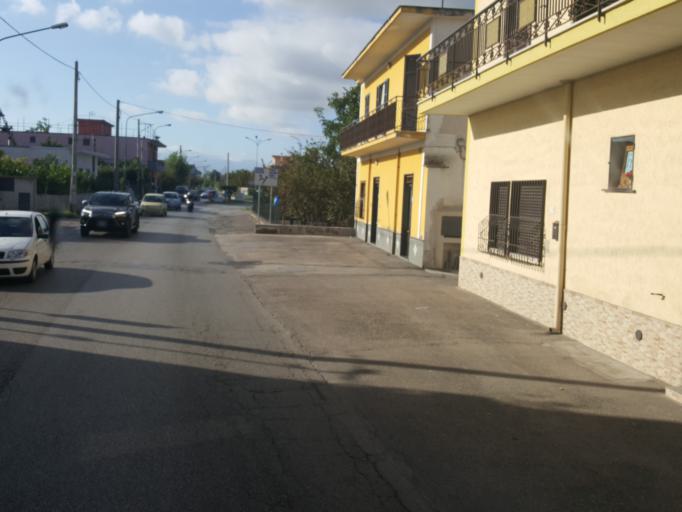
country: IT
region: Campania
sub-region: Provincia di Napoli
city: Nola
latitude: 40.9062
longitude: 14.5285
